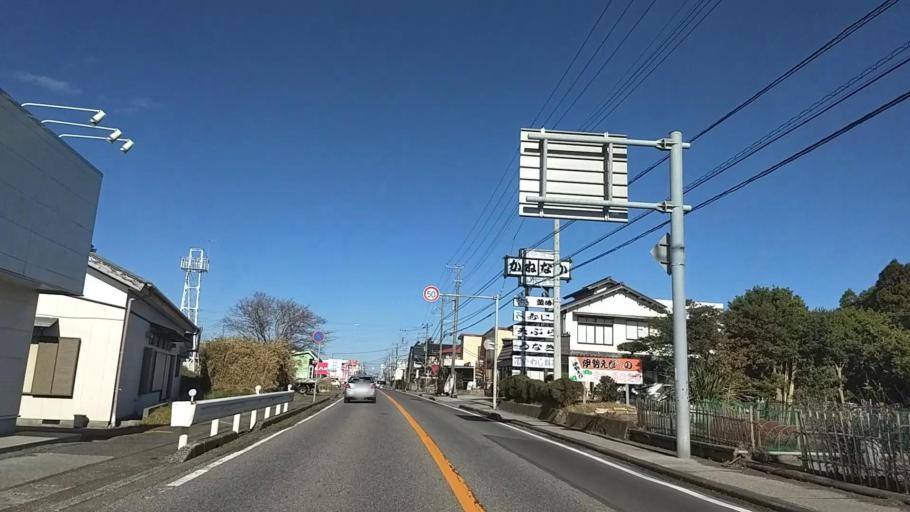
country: JP
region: Chiba
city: Ohara
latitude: 35.2368
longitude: 140.3901
